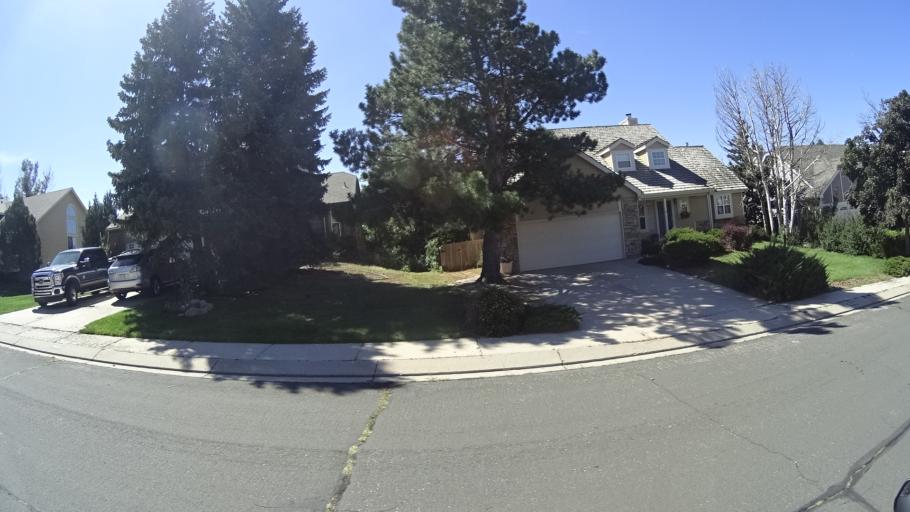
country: US
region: Colorado
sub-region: El Paso County
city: Black Forest
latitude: 38.9434
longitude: -104.7538
